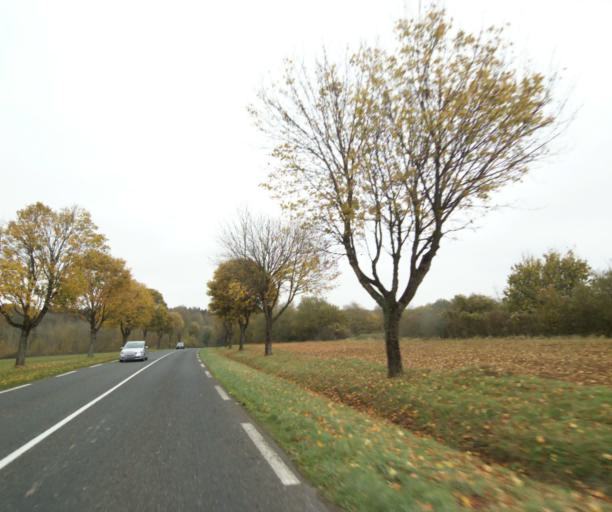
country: FR
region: Lorraine
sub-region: Departement de Meurthe-et-Moselle
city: Briey
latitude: 49.2685
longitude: 5.9529
